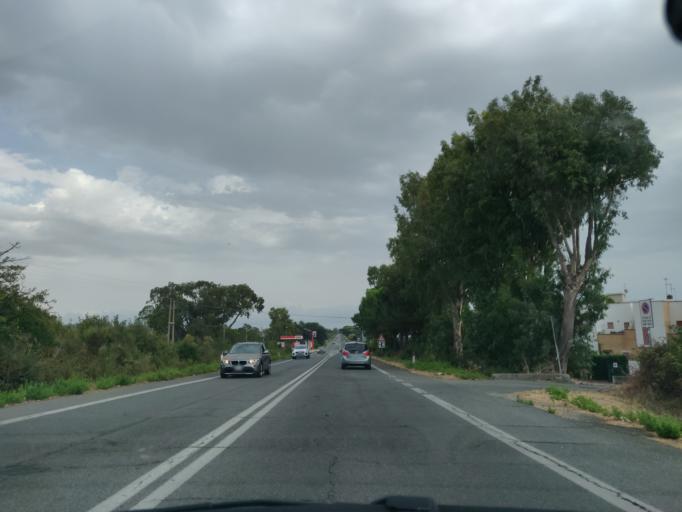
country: IT
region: Latium
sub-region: Citta metropolitana di Roma Capitale
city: Santa Marinella
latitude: 42.0300
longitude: 11.9393
